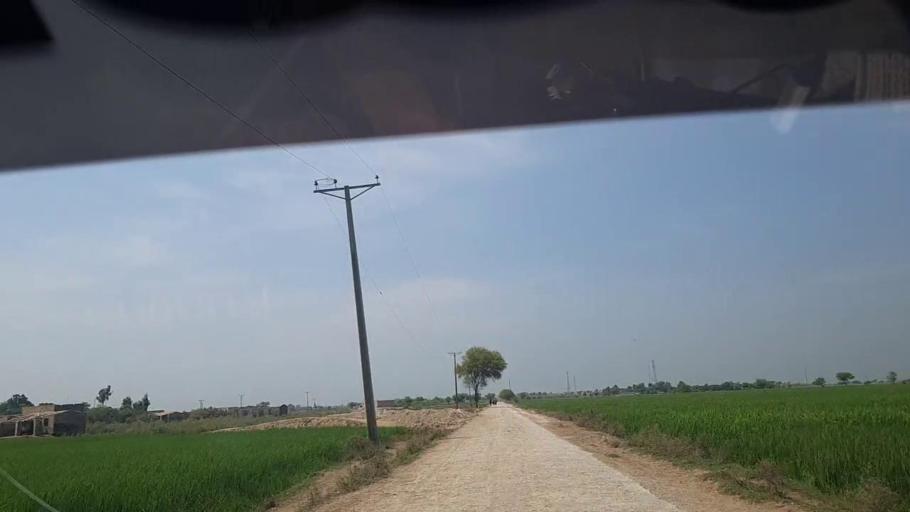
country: PK
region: Sindh
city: Thul
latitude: 28.1747
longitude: 68.7414
